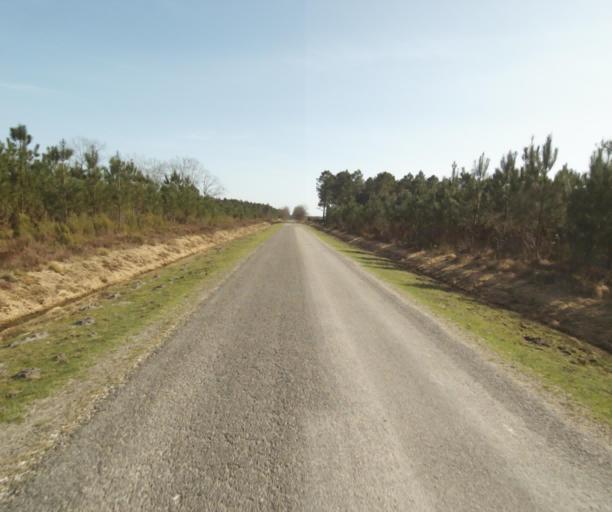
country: FR
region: Aquitaine
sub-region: Departement des Landes
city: Roquefort
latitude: 44.1722
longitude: -0.1764
